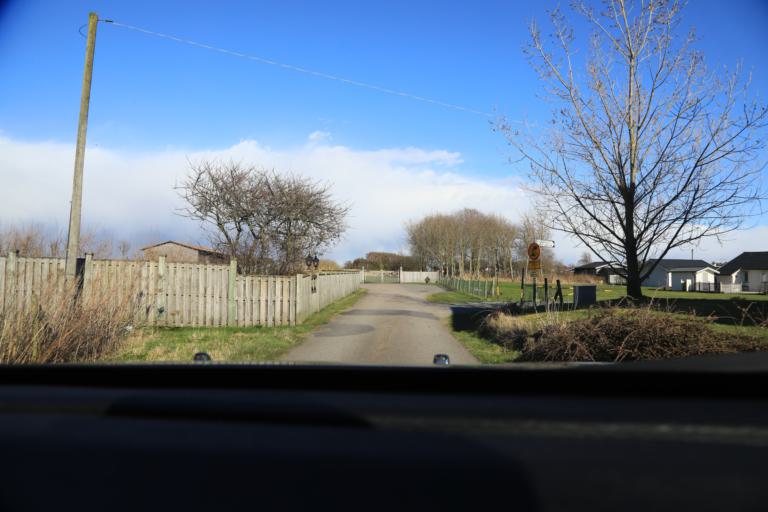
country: SE
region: Halland
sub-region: Varbergs Kommun
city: Traslovslage
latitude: 57.0708
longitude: 12.2760
